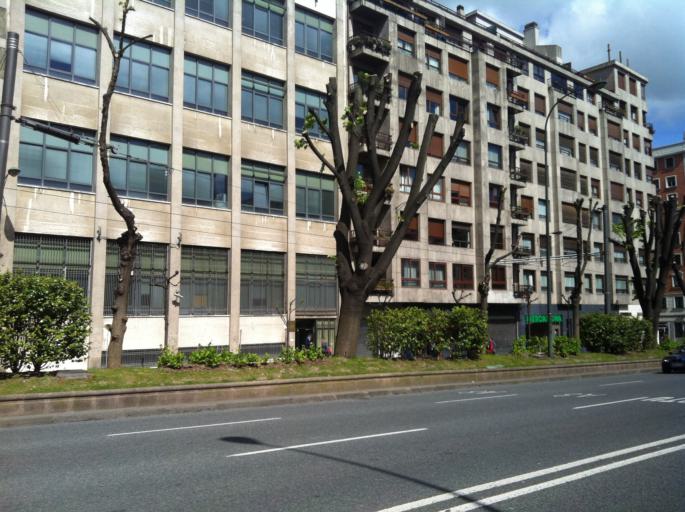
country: ES
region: Basque Country
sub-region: Bizkaia
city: Bilbao
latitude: 43.2615
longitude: -2.9468
